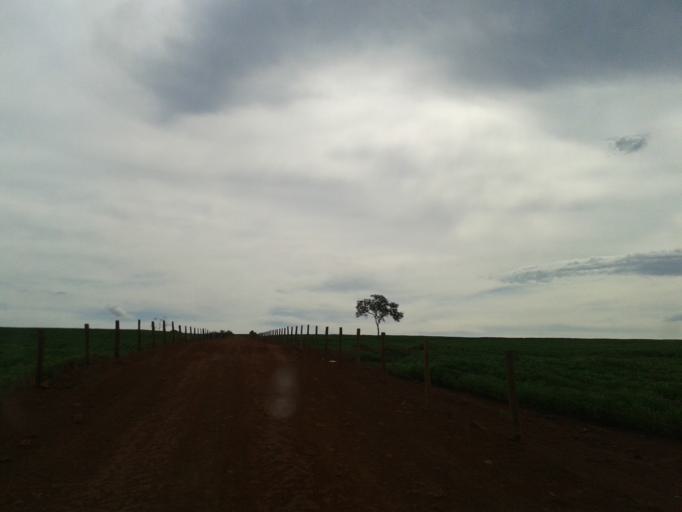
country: BR
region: Minas Gerais
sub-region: Centralina
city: Centralina
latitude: -18.6619
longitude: -49.3436
